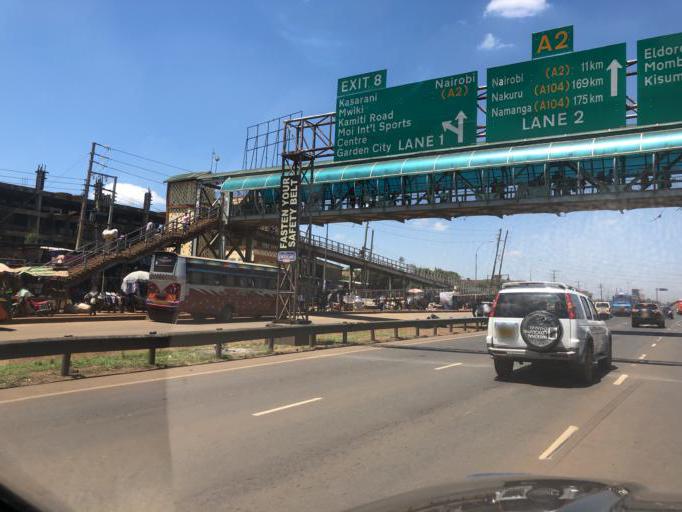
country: KE
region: Kiambu
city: Kiambu
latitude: -1.2167
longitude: 36.8948
